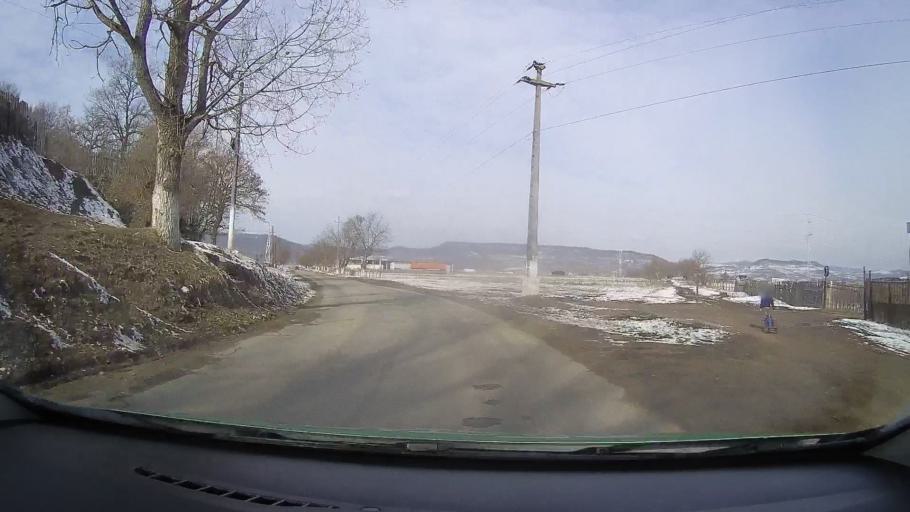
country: RO
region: Sibiu
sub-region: Comuna Laslea
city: Laslea
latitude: 46.2139
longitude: 24.6637
